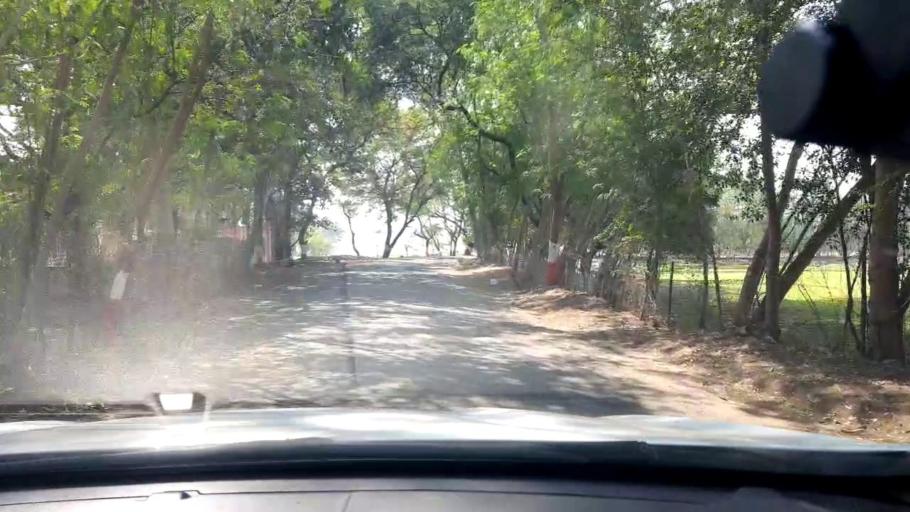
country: IN
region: Maharashtra
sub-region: Pune Division
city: Shivaji Nagar
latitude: 18.5457
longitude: 73.8592
